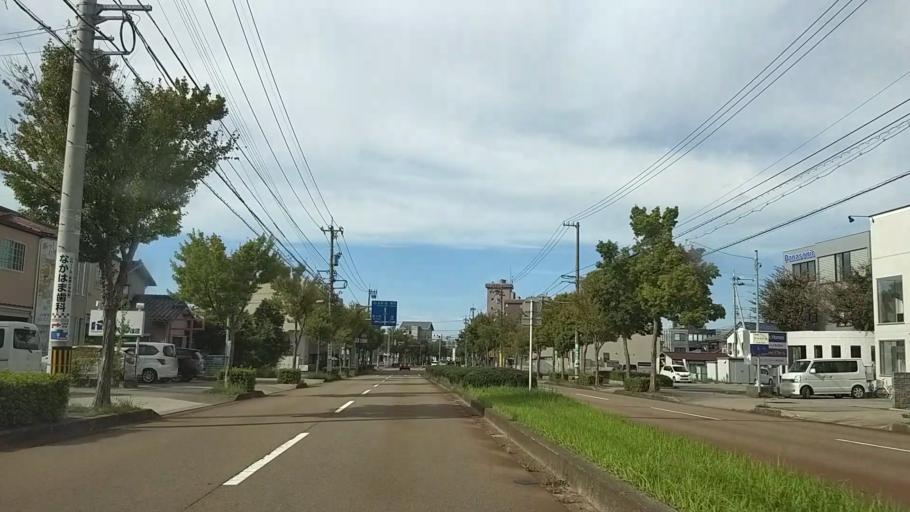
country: JP
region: Ishikawa
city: Nonoichi
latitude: 36.5278
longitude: 136.6385
